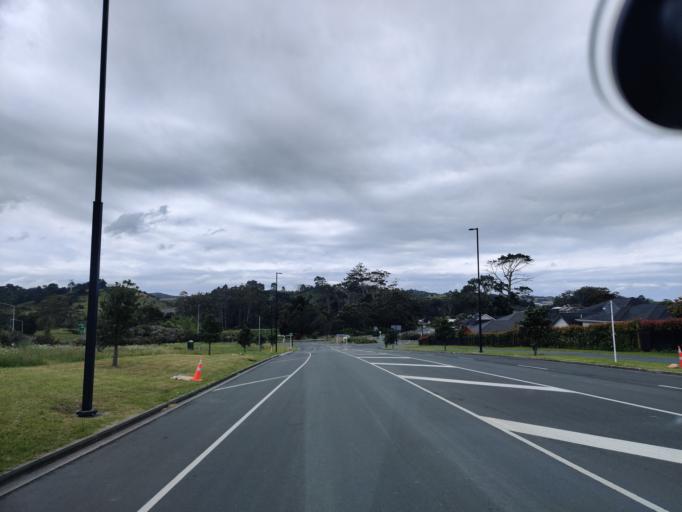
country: NZ
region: Auckland
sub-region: Auckland
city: Rothesay Bay
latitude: -36.6031
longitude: 174.6631
